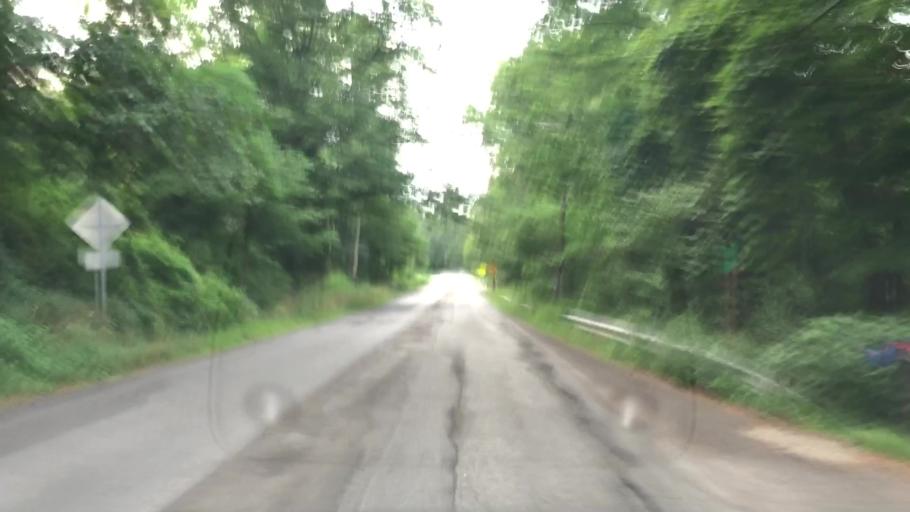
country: US
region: New York
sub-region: Erie County
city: East Aurora
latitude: 42.7858
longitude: -78.6048
